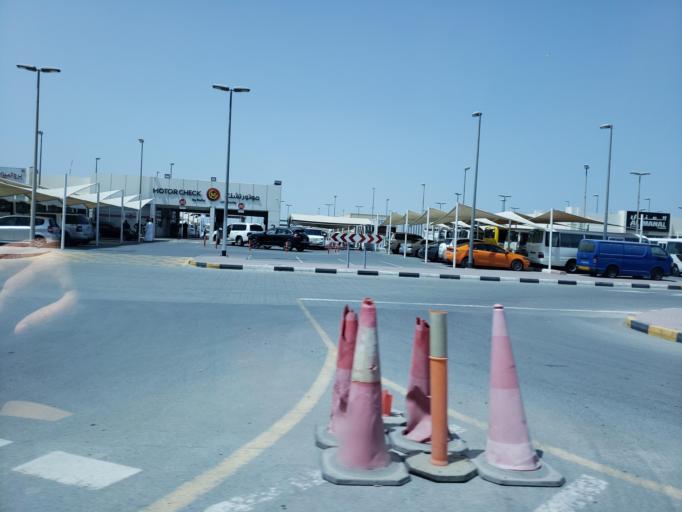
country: AE
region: Ash Shariqah
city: Sharjah
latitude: 25.3412
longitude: 55.4802
